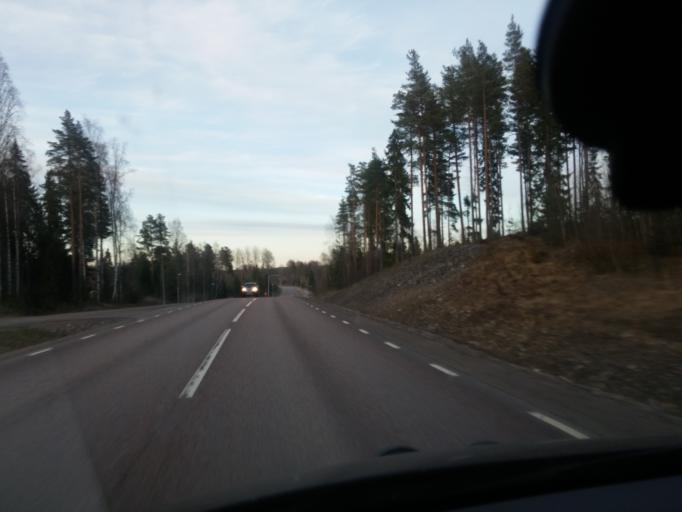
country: SE
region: Dalarna
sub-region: Borlange Kommun
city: Borlaenge
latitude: 60.5646
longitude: 15.4390
